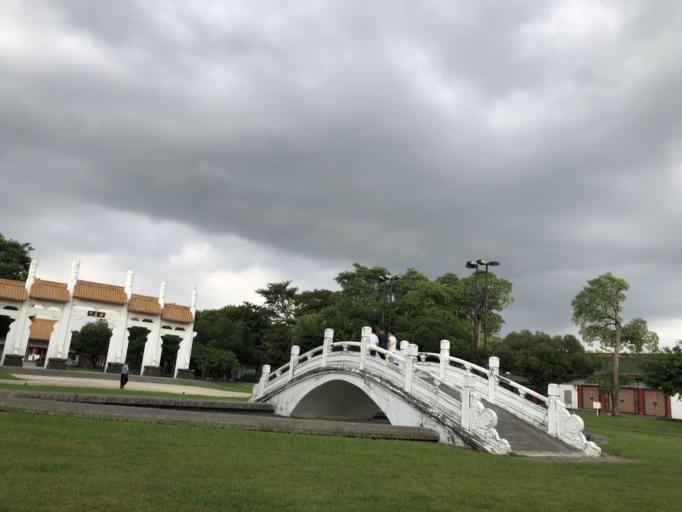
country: TW
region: Kaohsiung
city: Kaohsiung
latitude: 22.6876
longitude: 120.2980
